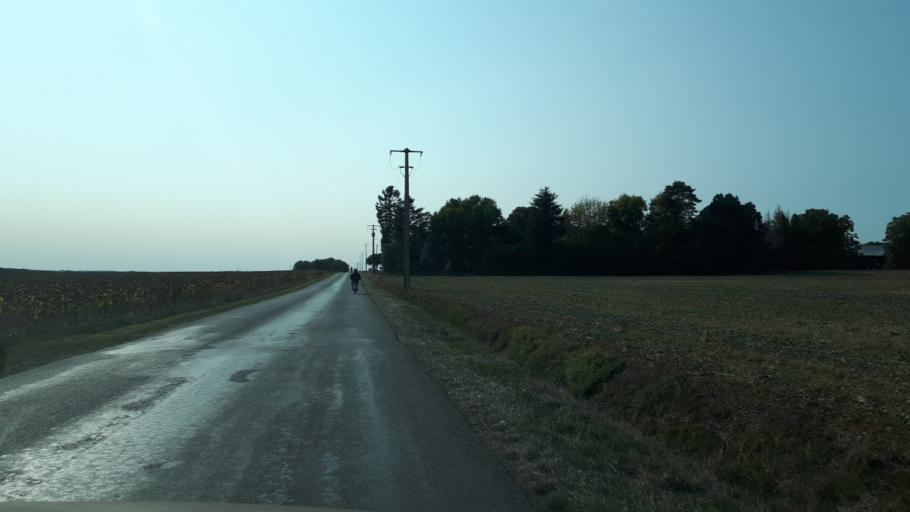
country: FR
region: Centre
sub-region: Departement du Cher
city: Rians
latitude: 47.1848
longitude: 2.6948
